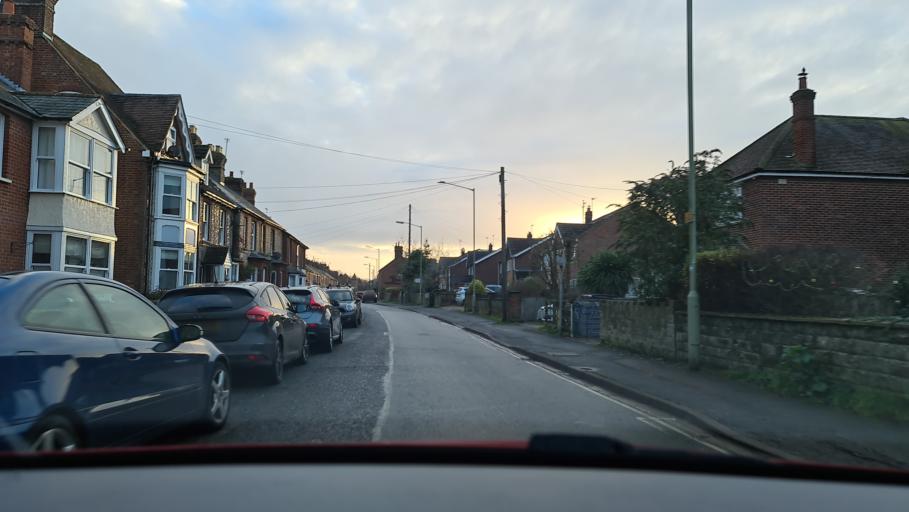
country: GB
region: England
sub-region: Oxfordshire
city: Thame
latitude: 51.7423
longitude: -0.9689
